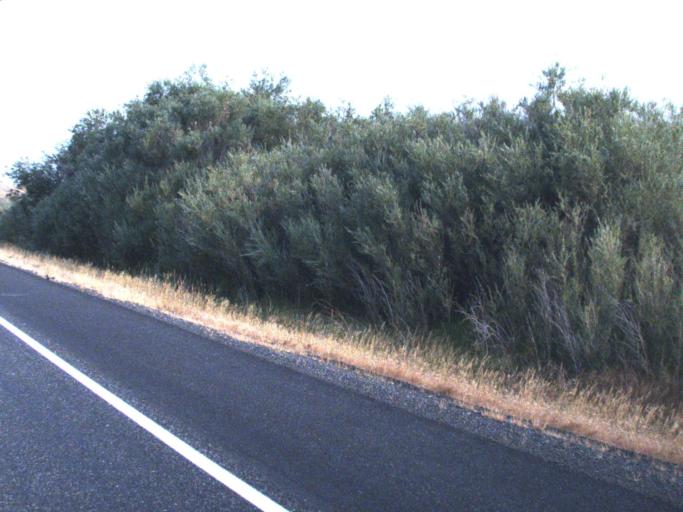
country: US
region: Washington
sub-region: Kittitas County
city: Ellensburg
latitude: 47.0906
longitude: -120.6535
